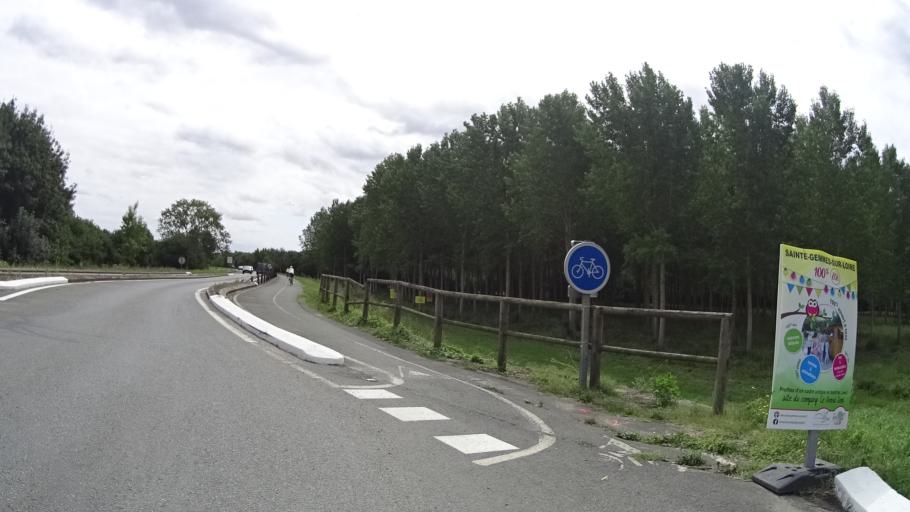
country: FR
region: Pays de la Loire
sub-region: Departement de Maine-et-Loire
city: Bouchemaine
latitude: 47.4196
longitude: -0.6065
